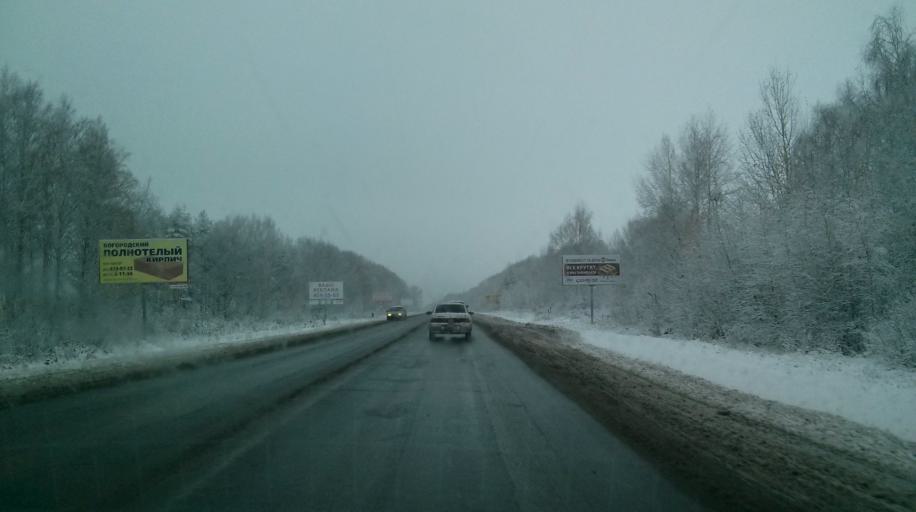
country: RU
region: Nizjnij Novgorod
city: Burevestnik
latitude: 56.1605
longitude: 43.7170
